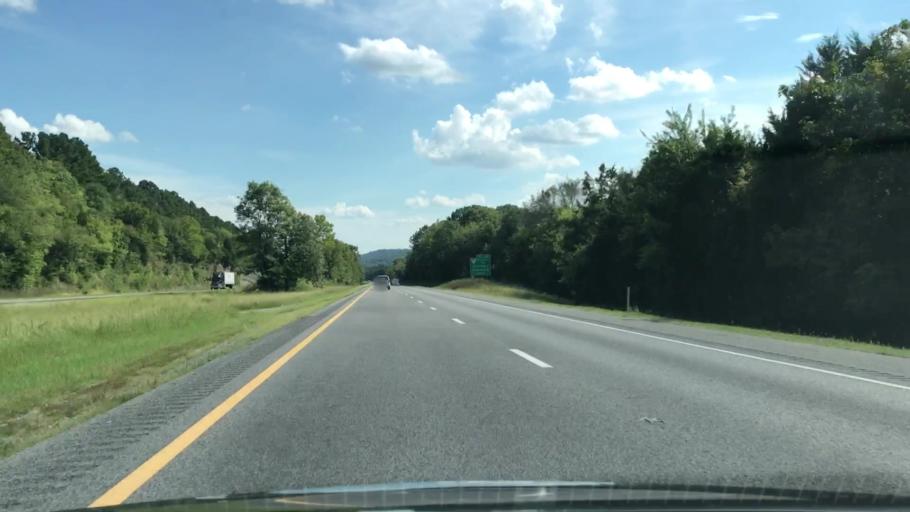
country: US
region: Tennessee
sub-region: Marshall County
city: Lewisburg
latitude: 35.4672
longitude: -86.8873
